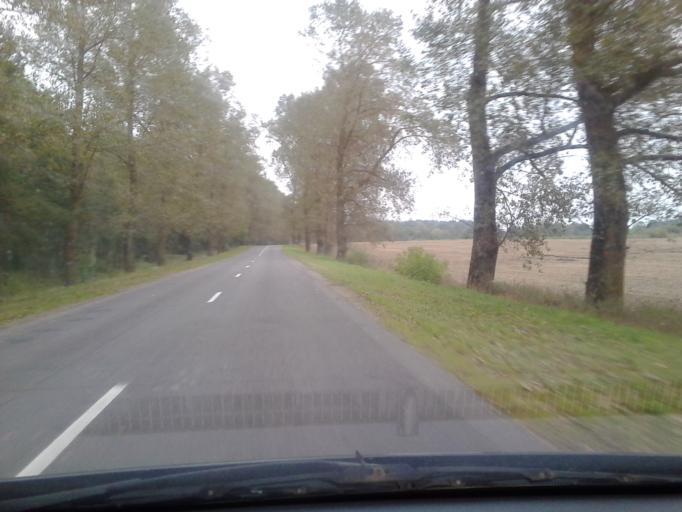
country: BY
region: Vitebsk
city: Pastavy
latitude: 55.1556
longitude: 26.9766
